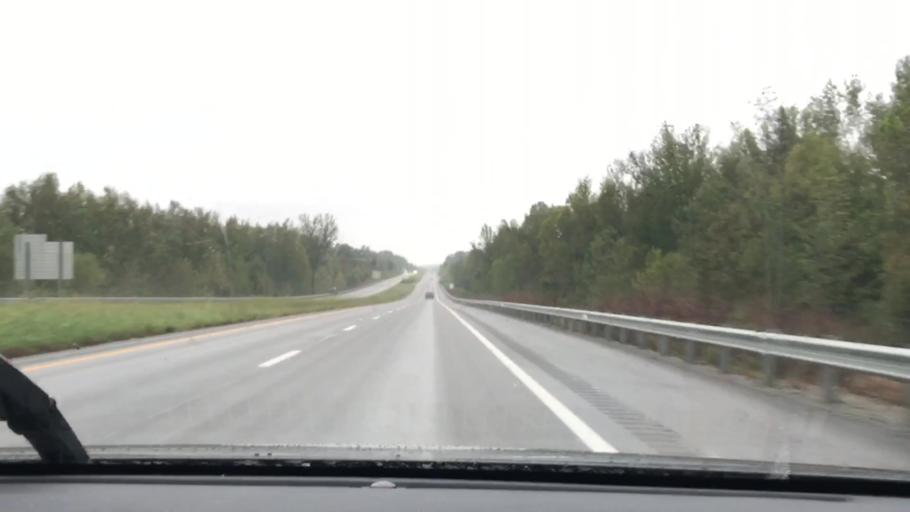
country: US
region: Kentucky
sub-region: Hopkins County
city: Nortonville
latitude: 37.1880
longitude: -87.4435
